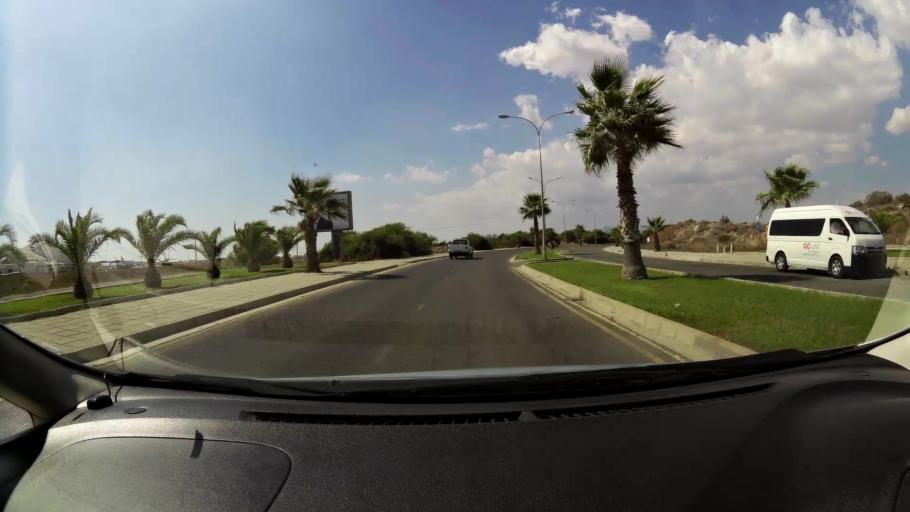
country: CY
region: Larnaka
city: Larnaca
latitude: 34.8907
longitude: 33.6336
